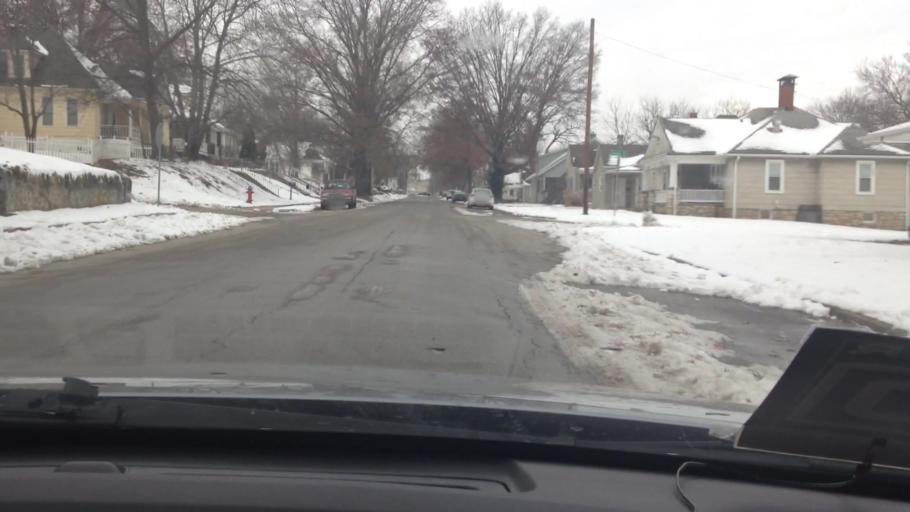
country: US
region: Kansas
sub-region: Leavenworth County
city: Leavenworth
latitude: 39.3247
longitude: -94.9348
